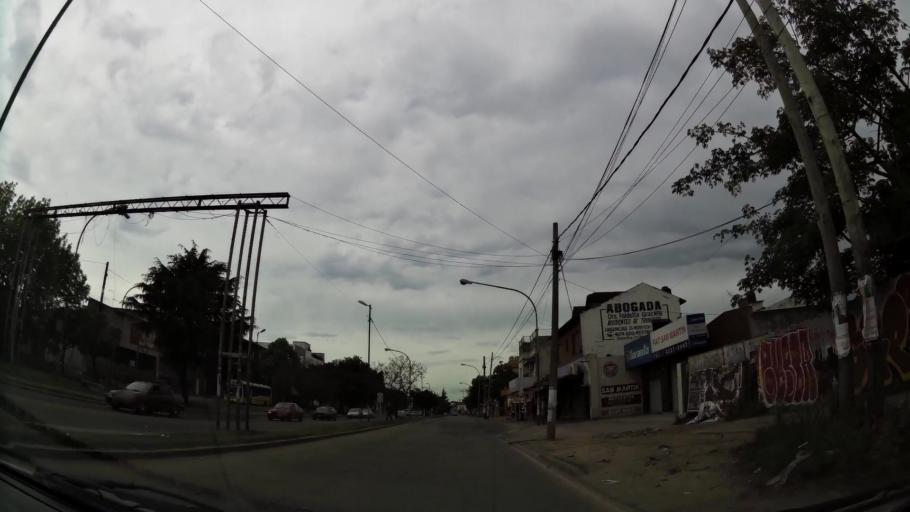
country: AR
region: Buenos Aires
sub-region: Partido de Quilmes
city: Quilmes
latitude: -34.7899
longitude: -58.2788
